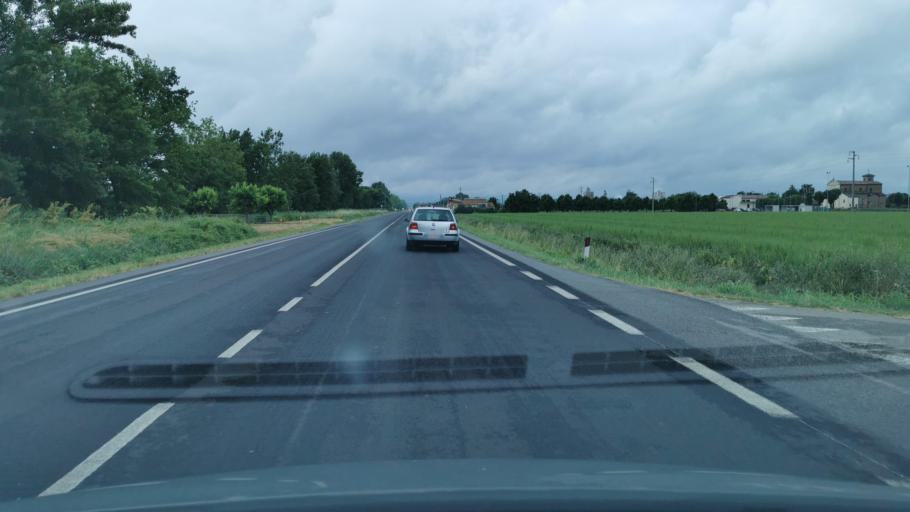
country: IT
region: Emilia-Romagna
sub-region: Provincia di Ravenna
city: Granarolo
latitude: 44.3386
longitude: 11.9182
